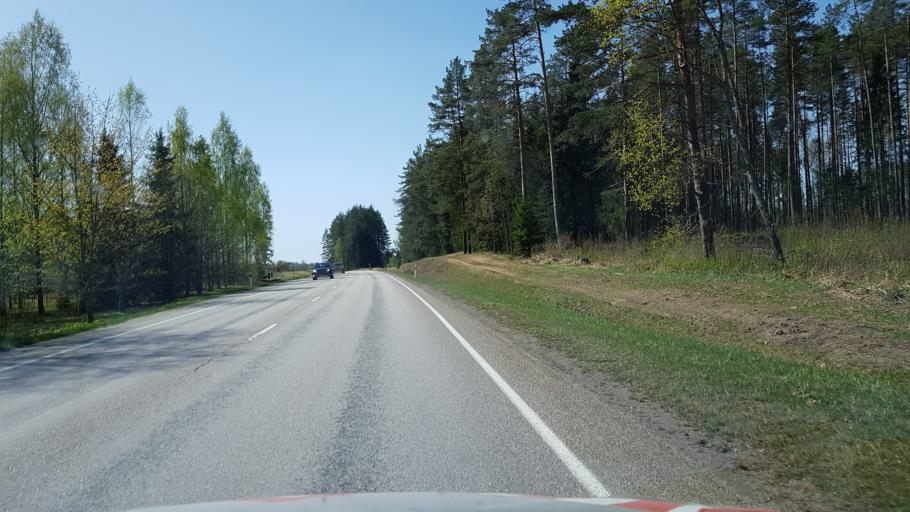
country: EE
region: Valgamaa
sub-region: Valga linn
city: Valga
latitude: 57.8160
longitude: 26.0440
